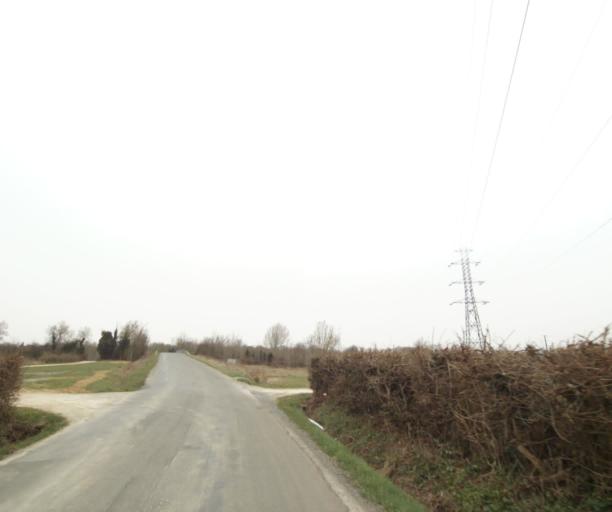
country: FR
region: Poitou-Charentes
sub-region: Departement des Deux-Sevres
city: Niort
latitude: 46.3015
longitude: -0.4782
